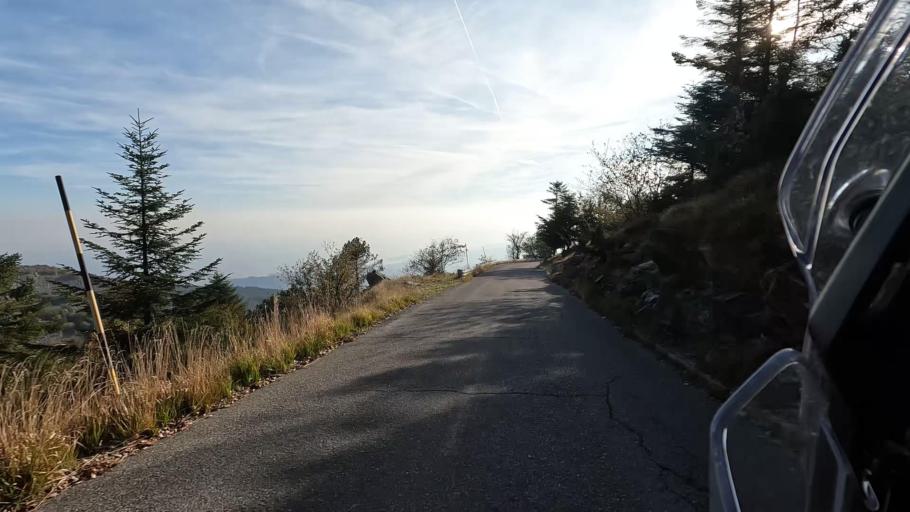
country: IT
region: Liguria
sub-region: Provincia di Savona
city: San Giovanni
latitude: 44.4291
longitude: 8.5494
